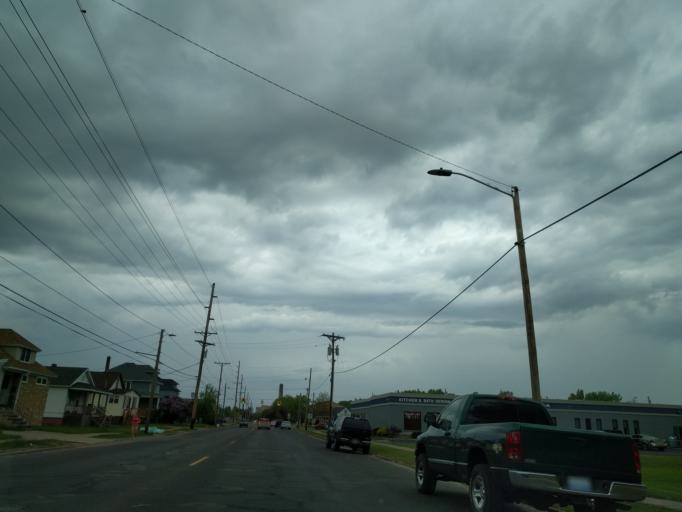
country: US
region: Michigan
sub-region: Marquette County
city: Marquette
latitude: 46.5627
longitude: -87.3961
